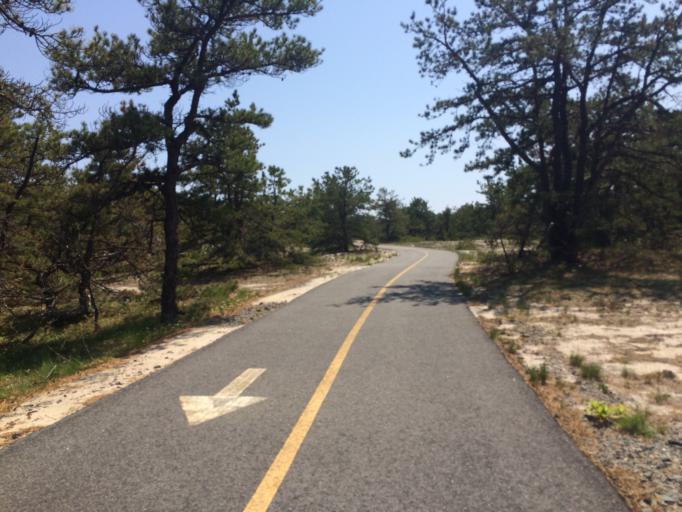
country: US
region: Massachusetts
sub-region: Barnstable County
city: Provincetown
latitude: 42.0651
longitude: -70.2155
